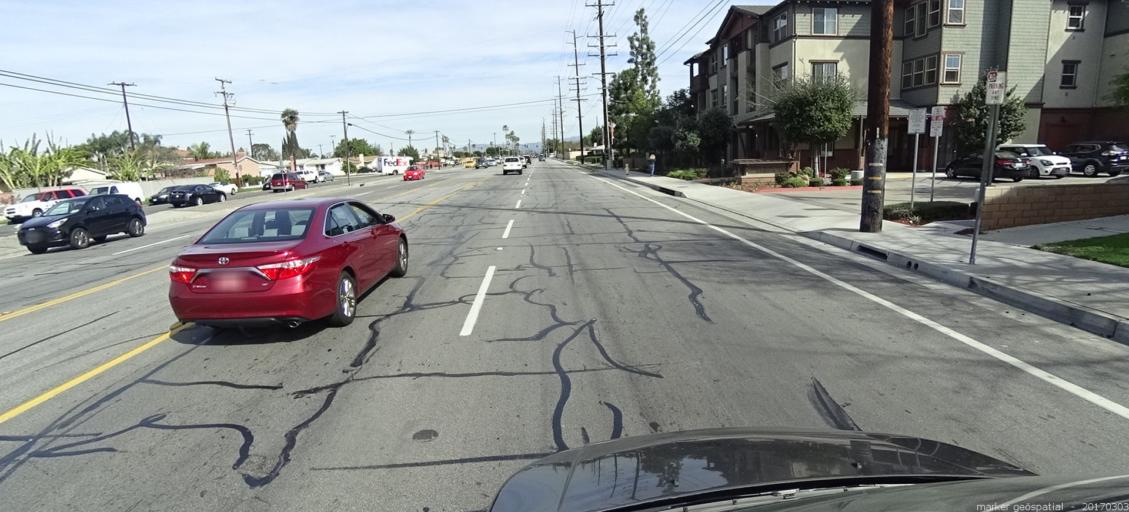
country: US
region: California
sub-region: Orange County
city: Stanton
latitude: 33.8176
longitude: -117.9662
